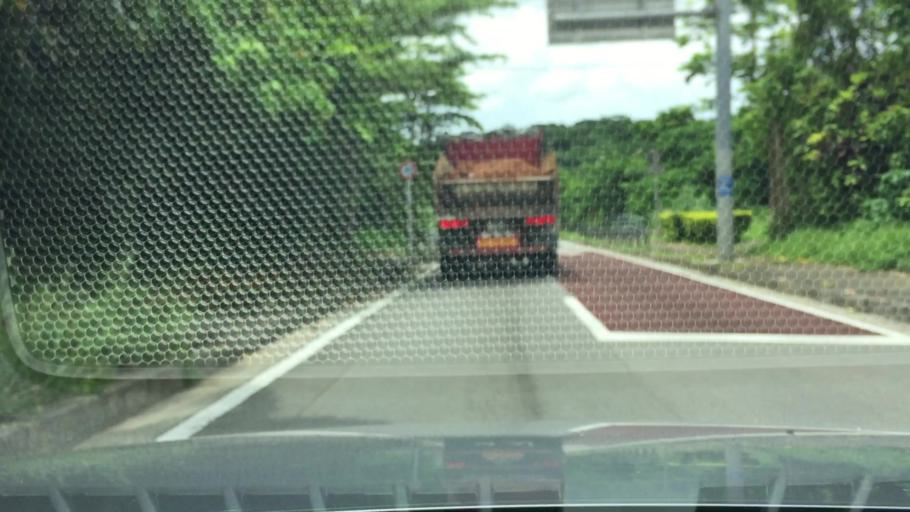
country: JP
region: Okinawa
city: Ishigaki
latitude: 24.4532
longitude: 124.2012
